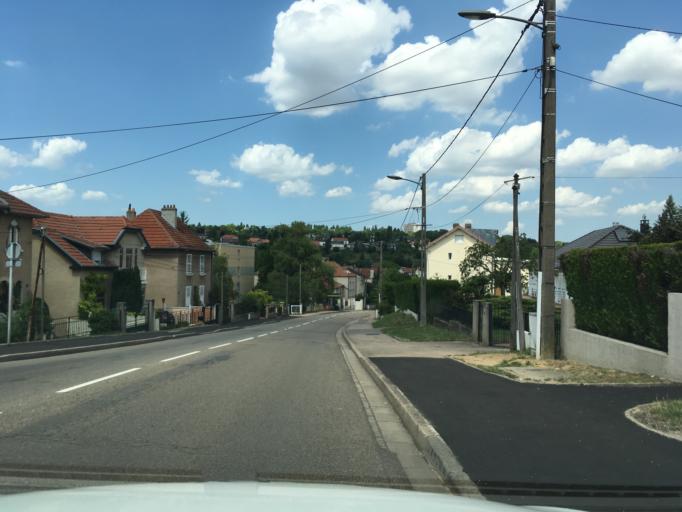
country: FR
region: Lorraine
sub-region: Departement de la Moselle
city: Saint-Julien-les-Metz
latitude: 49.1222
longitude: 6.2155
